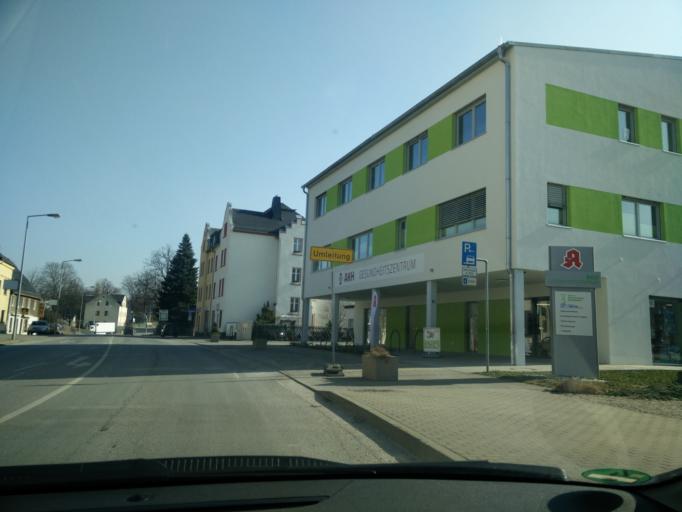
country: DE
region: Saxony
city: Hartmannsdorf
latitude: 50.8868
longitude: 12.7985
